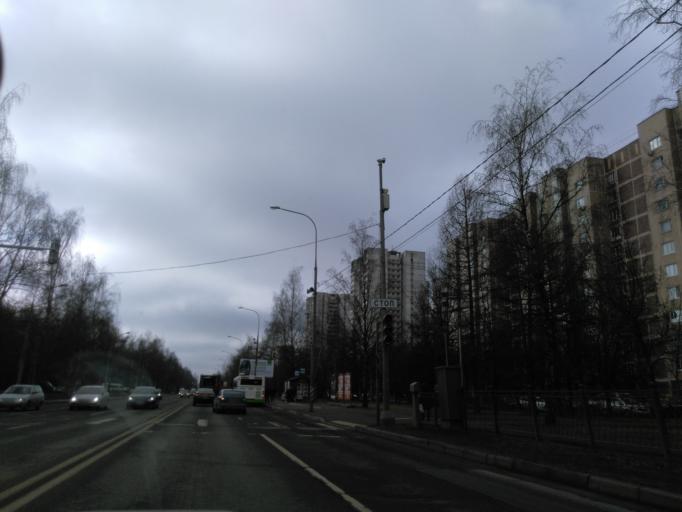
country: RU
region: Moskovskaya
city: Levoberezhnyy
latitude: 55.8631
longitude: 37.4483
